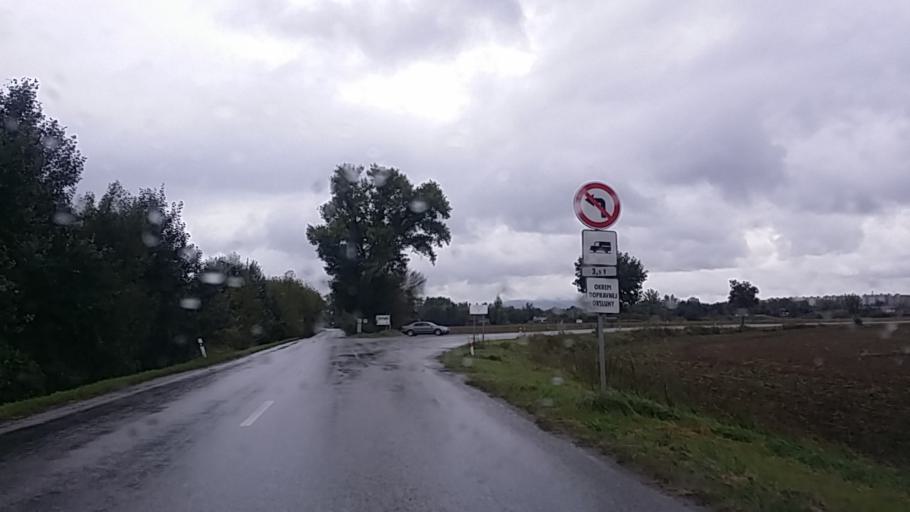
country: SK
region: Nitriansky
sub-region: Okres Nove Zamky
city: Sturovo
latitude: 47.8111
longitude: 18.7224
